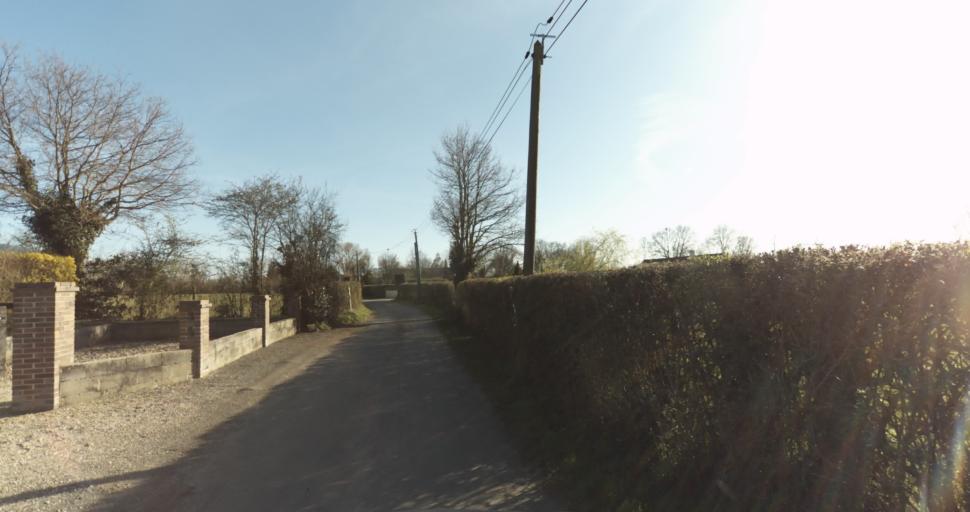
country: FR
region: Lower Normandy
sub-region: Departement du Calvados
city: Livarot
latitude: 48.9957
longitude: 0.1040
